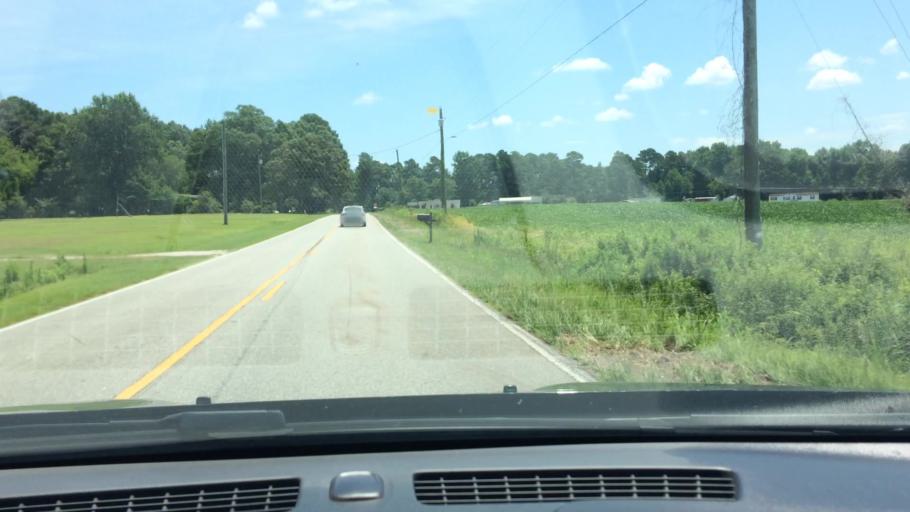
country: US
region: North Carolina
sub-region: Pitt County
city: Windsor
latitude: 35.5668
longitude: -77.2134
